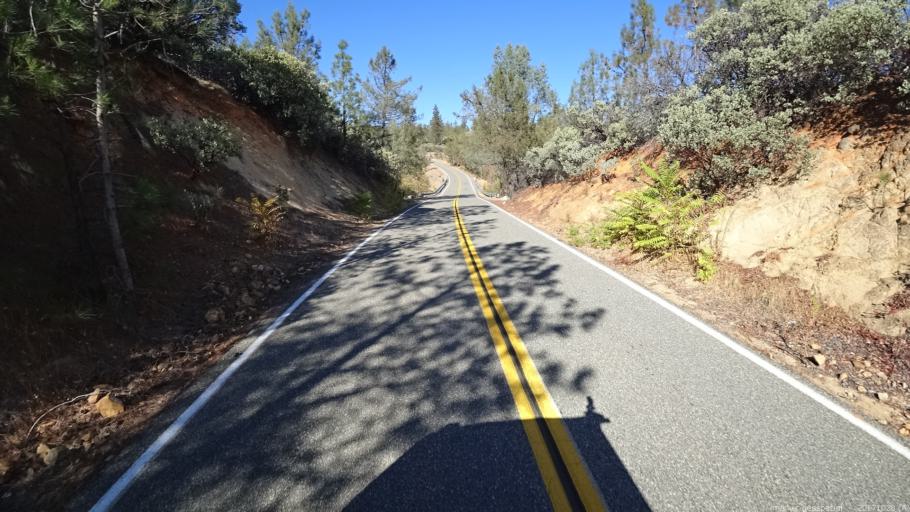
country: US
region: California
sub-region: Shasta County
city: Shasta
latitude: 40.6533
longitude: -122.4617
